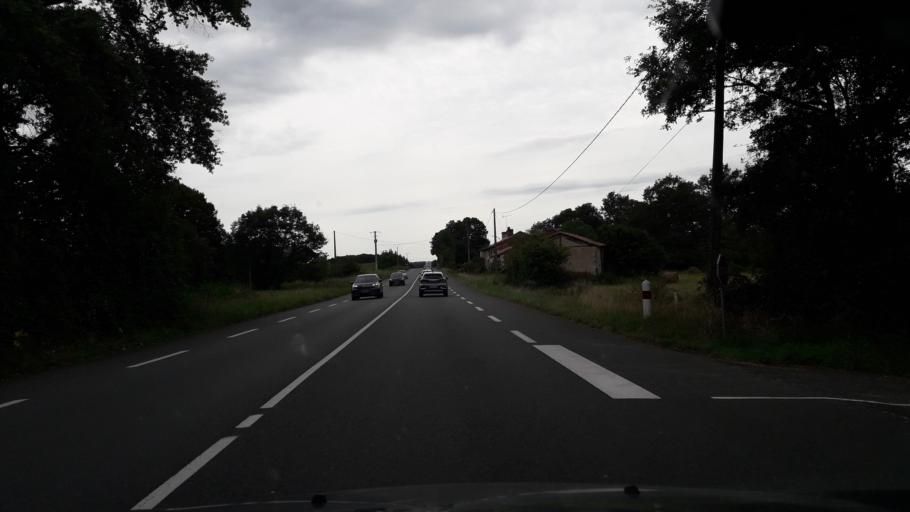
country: FR
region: Poitou-Charentes
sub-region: Departement de la Charente
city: Loubert
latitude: 45.9504
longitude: 0.5631
